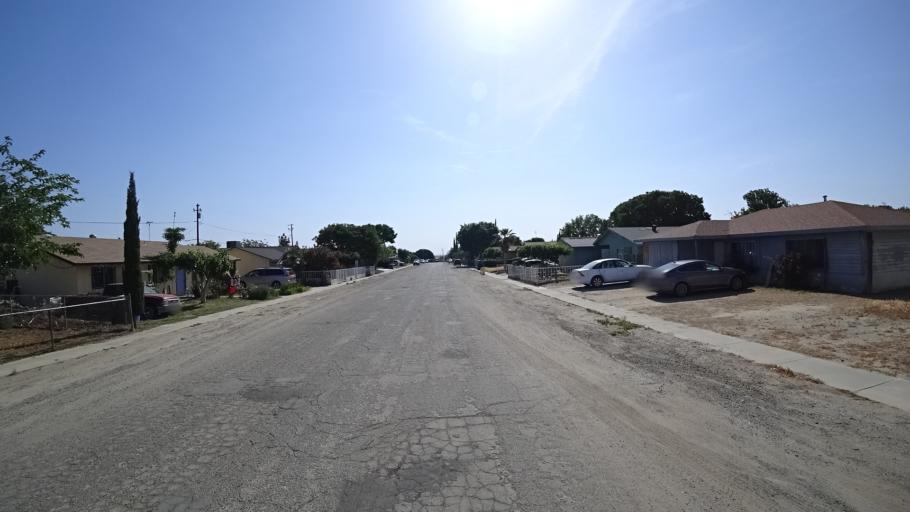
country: US
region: California
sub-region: Kings County
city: Kettleman City
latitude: 36.0110
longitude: -119.9638
